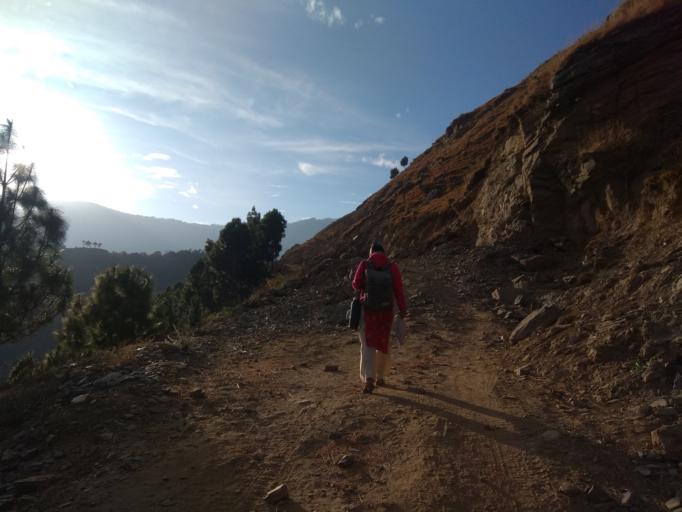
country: NP
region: Far Western
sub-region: Seti Zone
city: Achham
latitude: 29.2486
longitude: 81.6532
